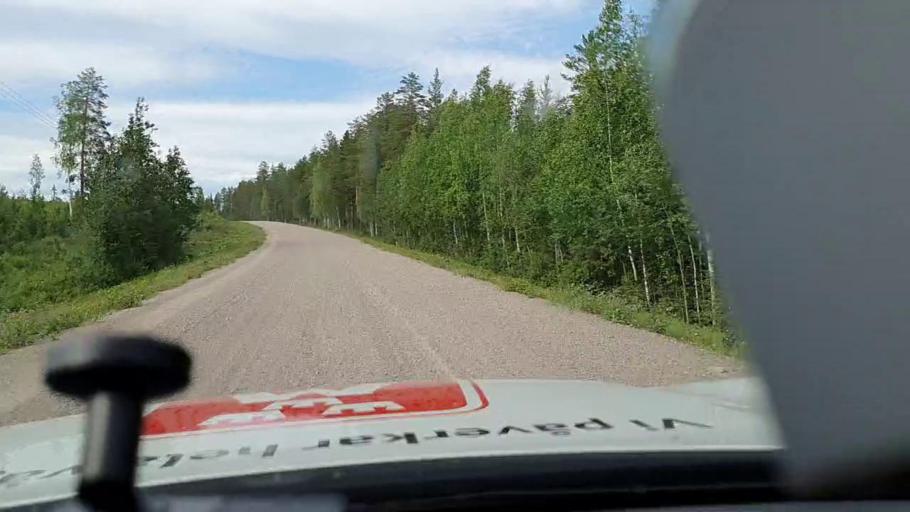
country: SE
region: Norrbotten
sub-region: Alvsbyns Kommun
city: AElvsbyn
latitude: 66.1294
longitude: 20.9984
